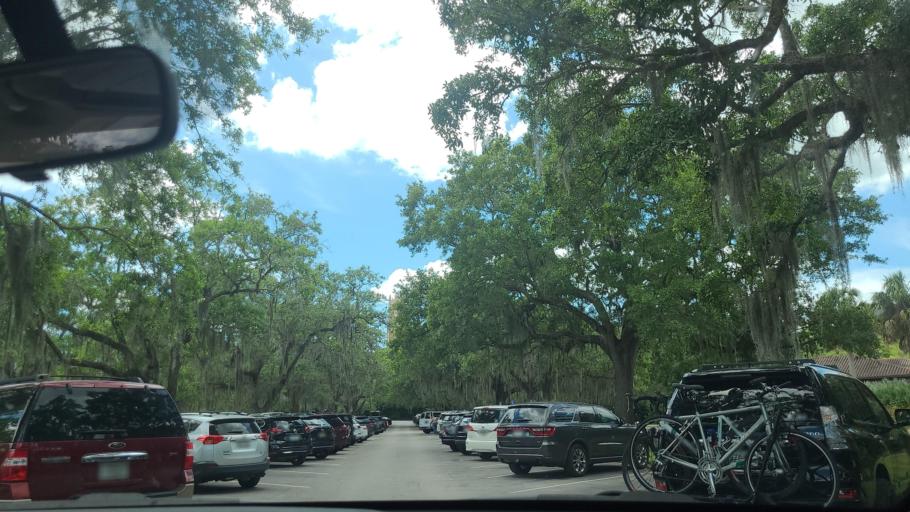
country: US
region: Florida
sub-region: Polk County
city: Lake Wales
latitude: 27.9378
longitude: -81.5748
